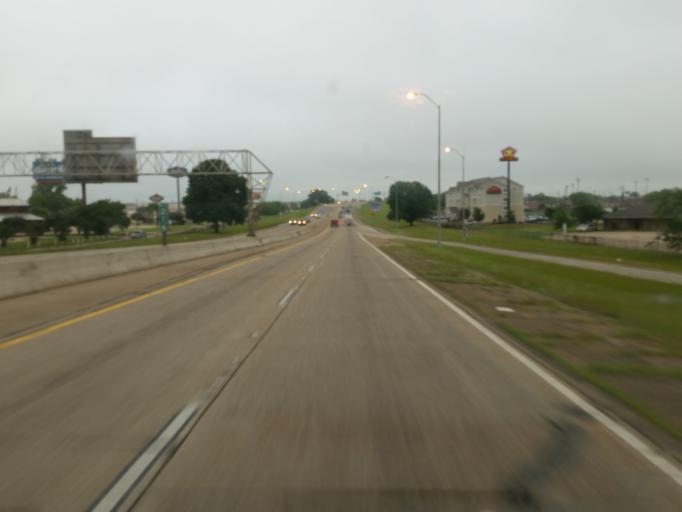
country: US
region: Louisiana
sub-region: Bossier Parish
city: Bossier City
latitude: 32.5189
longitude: -93.7085
